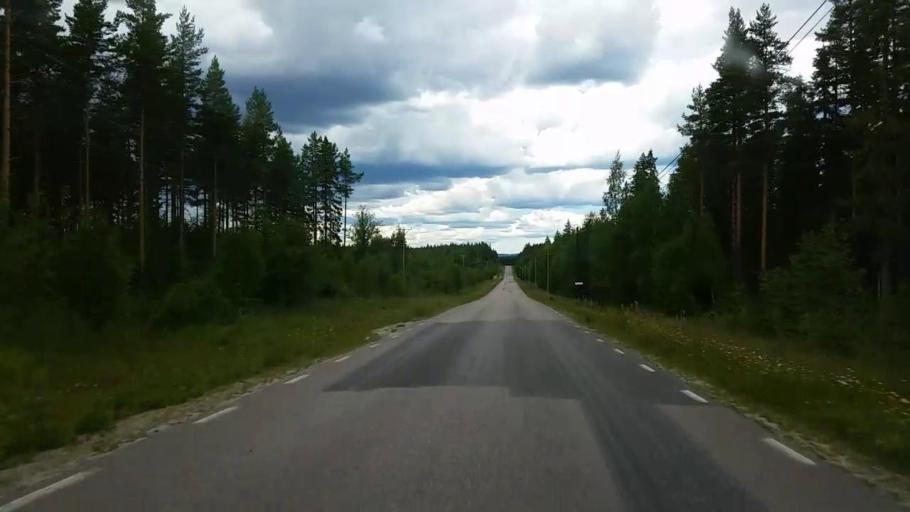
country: SE
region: Gaevleborg
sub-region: Ovanakers Kommun
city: Edsbyn
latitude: 61.4205
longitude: 15.9000
